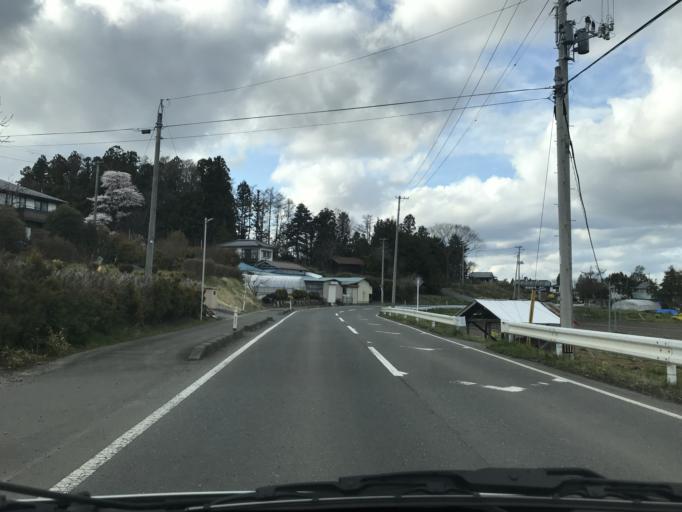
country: JP
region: Miyagi
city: Wakuya
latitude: 38.6435
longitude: 141.2166
